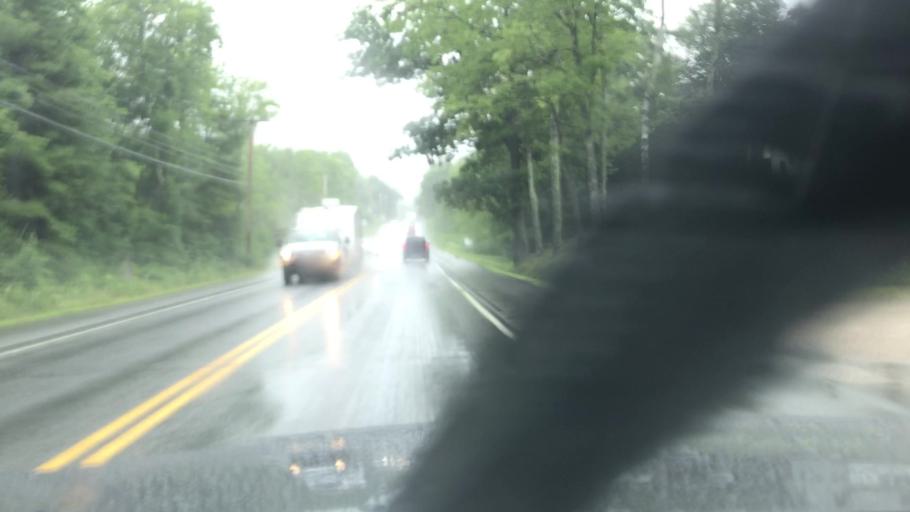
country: US
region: Maine
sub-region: York County
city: Kennebunk
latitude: 43.4285
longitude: -70.5106
